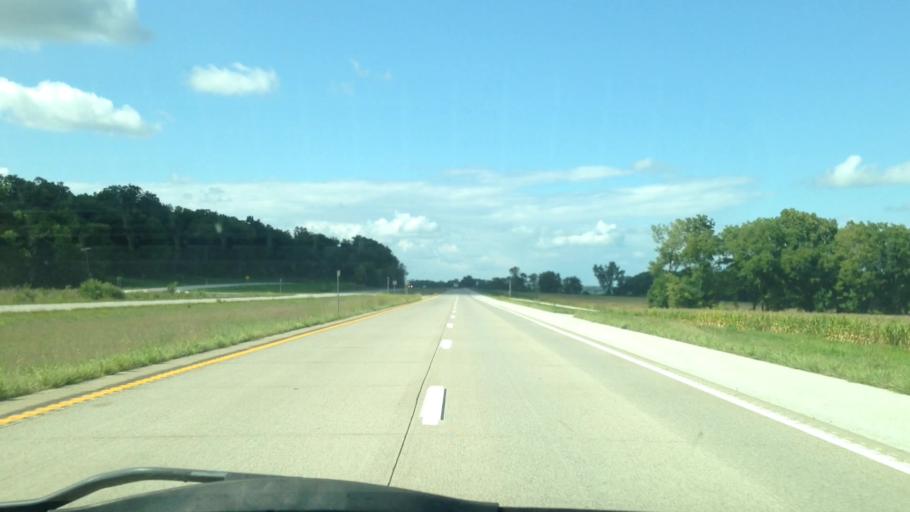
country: US
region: Missouri
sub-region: Lewis County
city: Canton
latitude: 40.2147
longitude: -91.5249
